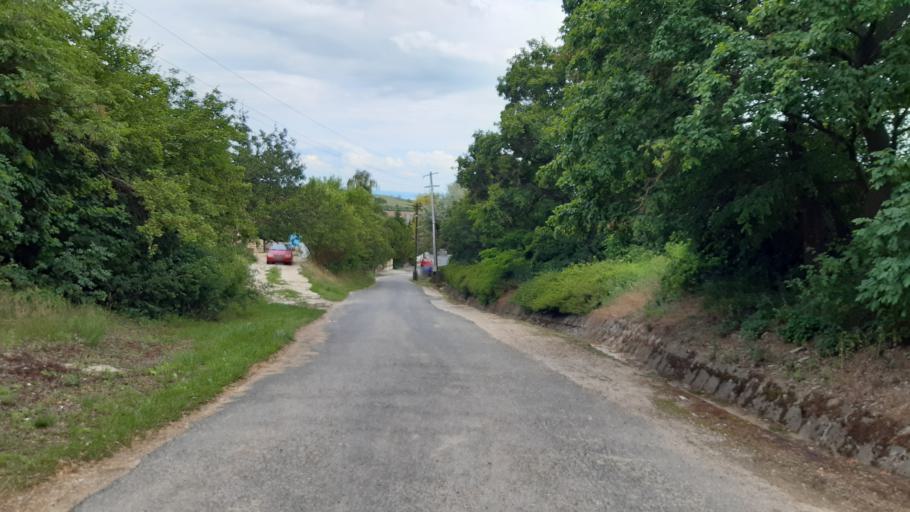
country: HU
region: Veszprem
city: Zanka
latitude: 46.9356
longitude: 17.6753
